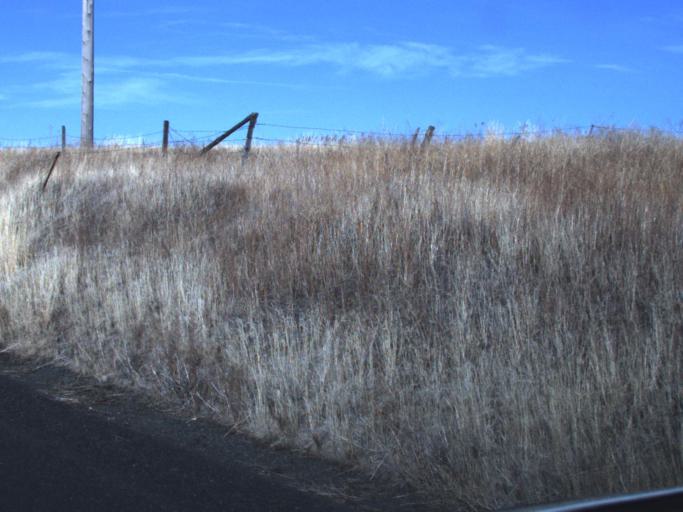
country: US
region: Washington
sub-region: Lincoln County
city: Davenport
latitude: 47.8098
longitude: -118.1784
